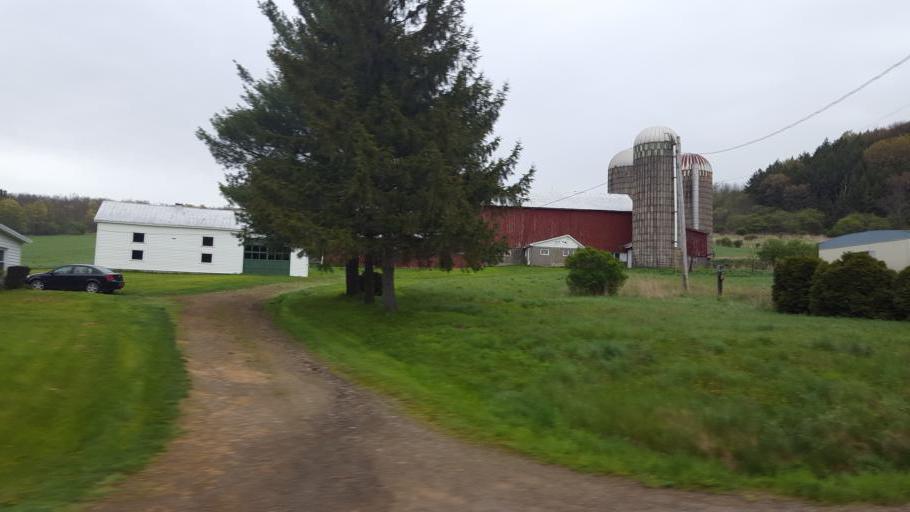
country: US
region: Pennsylvania
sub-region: Tioga County
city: Westfield
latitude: 42.0202
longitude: -77.4663
